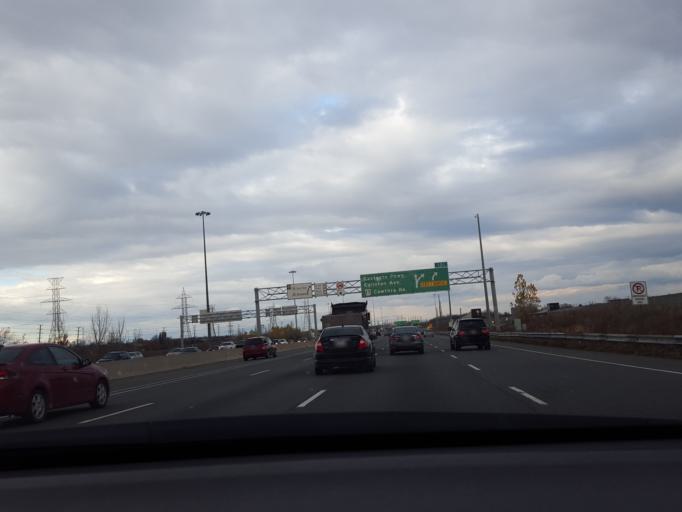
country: CA
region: Ontario
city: Mississauga
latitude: 43.6063
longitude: -79.6382
